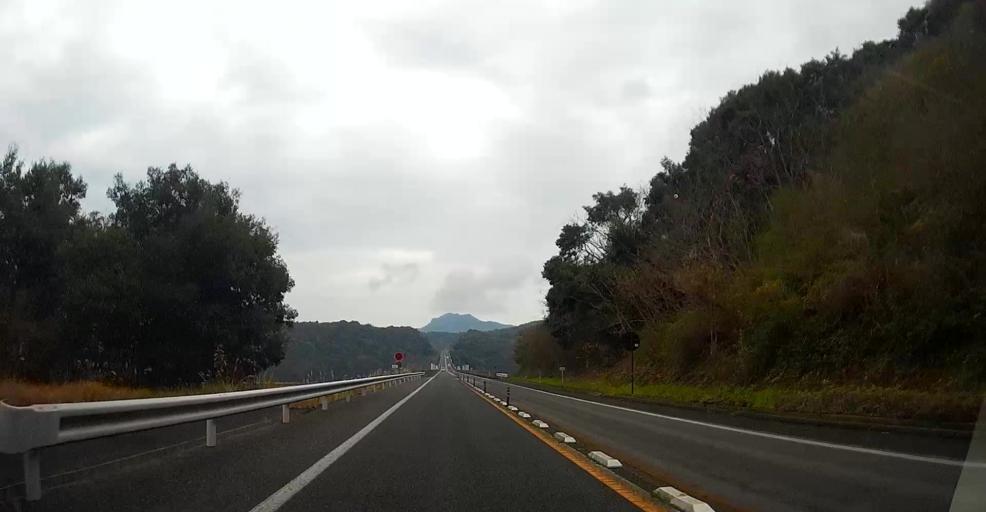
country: JP
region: Kumamoto
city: Hondo
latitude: 32.5073
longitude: 130.3710
